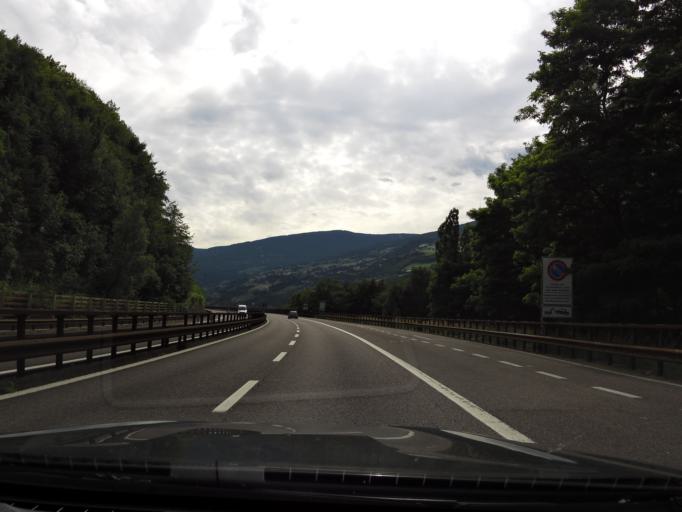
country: IT
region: Trentino-Alto Adige
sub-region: Bolzano
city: Chiusa
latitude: 46.6435
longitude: 11.5785
